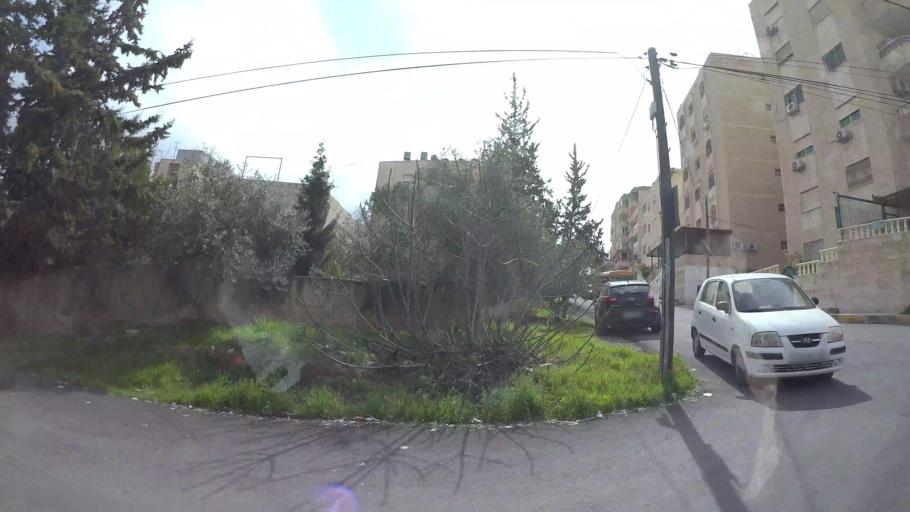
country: JO
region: Amman
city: Amman
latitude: 32.0009
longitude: 35.9339
